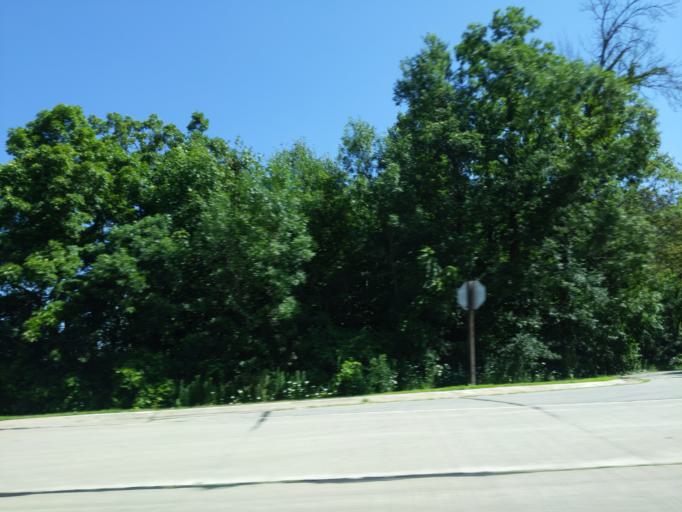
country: US
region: Wisconsin
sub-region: La Crosse County
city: La Crosse
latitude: 43.7290
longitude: -91.0893
